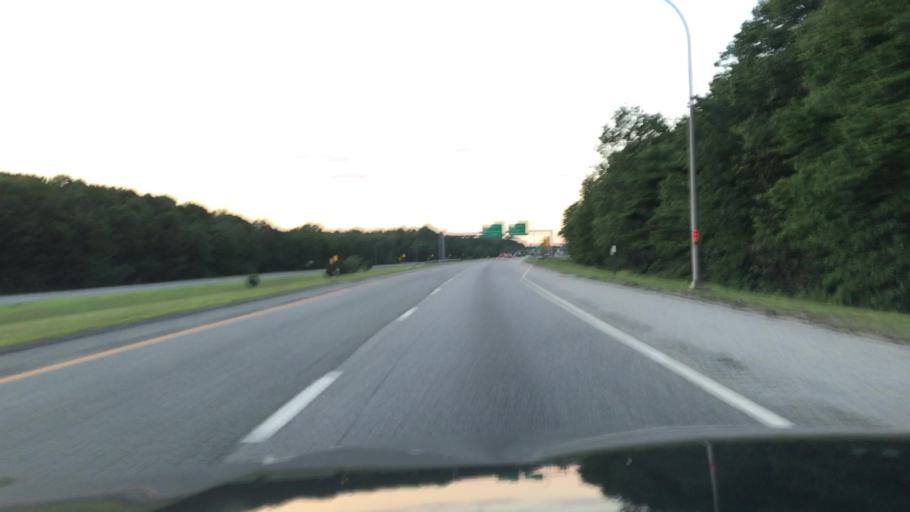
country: US
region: Rhode Island
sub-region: Kent County
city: West Greenwich
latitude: 41.5963
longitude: -71.6592
